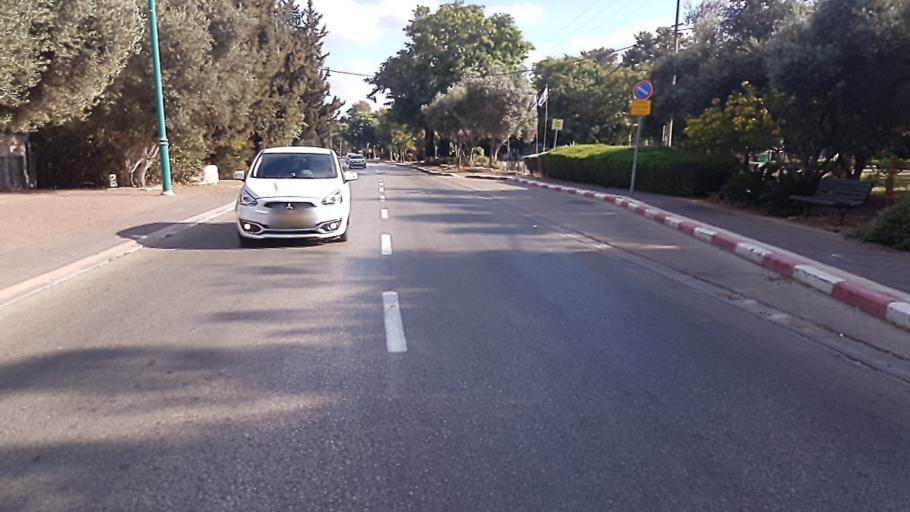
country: IL
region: Central District
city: Jaljulya
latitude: 32.1739
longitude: 34.9391
